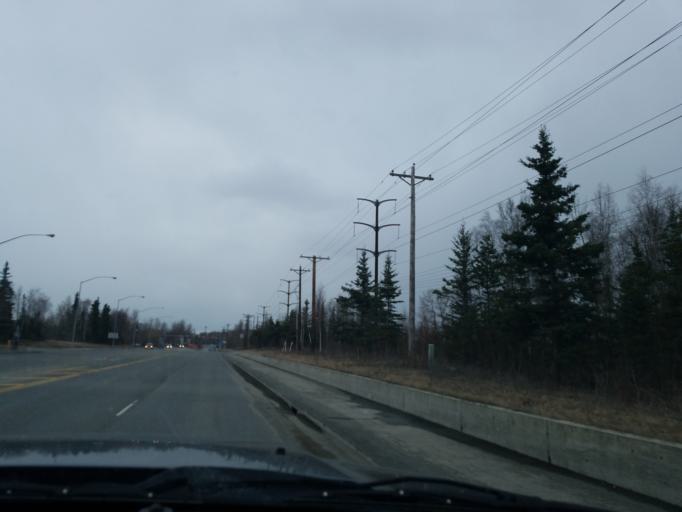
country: US
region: Alaska
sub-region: Anchorage Municipality
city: Anchorage
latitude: 61.1777
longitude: -149.8081
